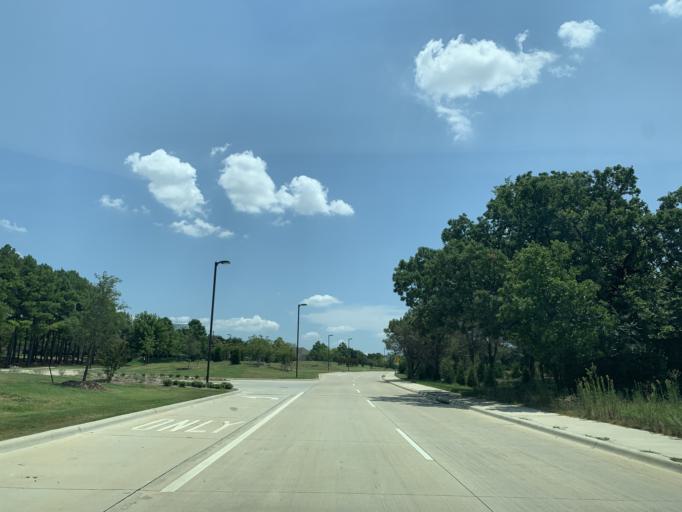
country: US
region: Texas
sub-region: Denton County
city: Trophy Club
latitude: 32.9742
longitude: -97.1559
